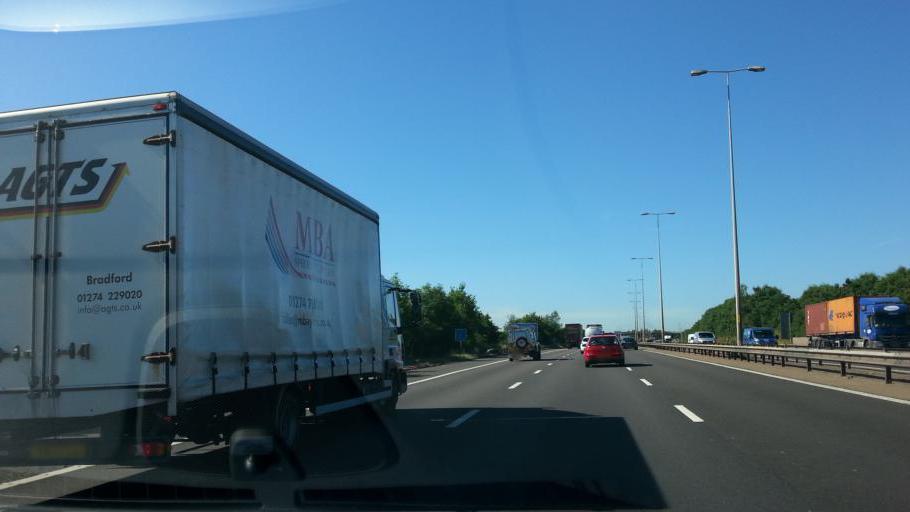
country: GB
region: England
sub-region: Worcestershire
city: Worcester
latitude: 52.1786
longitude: -2.1731
